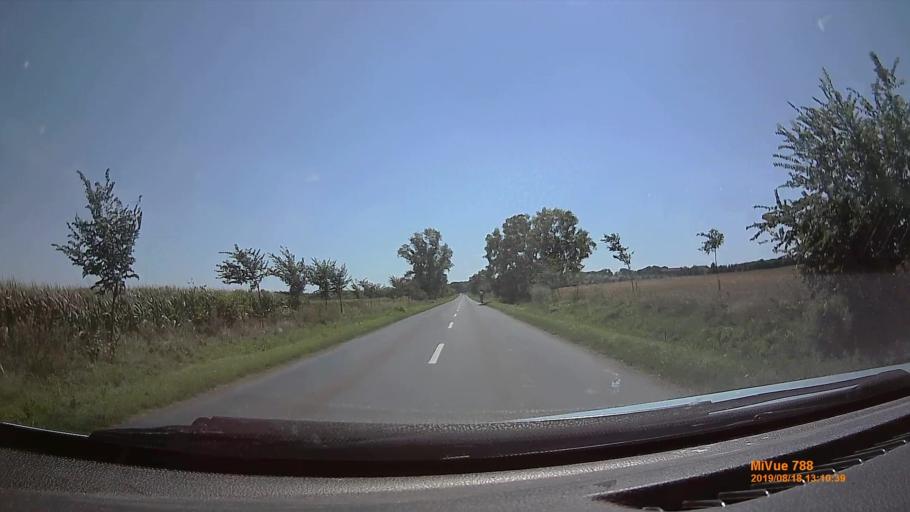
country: HU
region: Fejer
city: Kaloz
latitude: 46.9120
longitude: 18.5173
